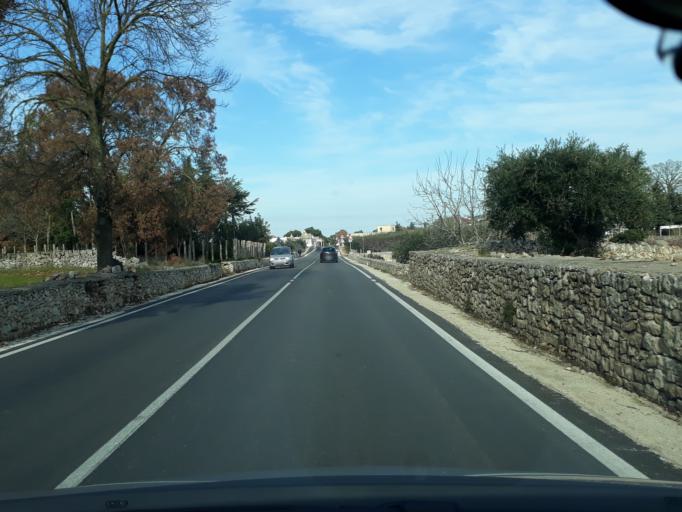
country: IT
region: Apulia
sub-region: Provincia di Bari
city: Locorotondo
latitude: 40.7729
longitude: 17.3349
